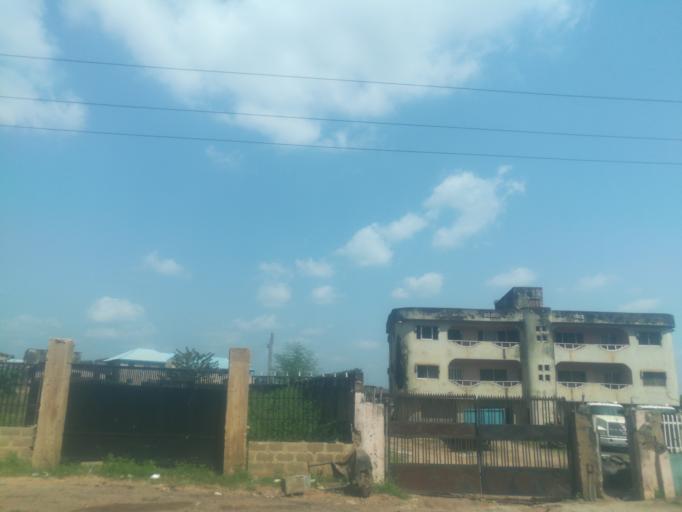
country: NG
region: Oyo
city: Moniya
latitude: 7.4954
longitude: 3.9145
